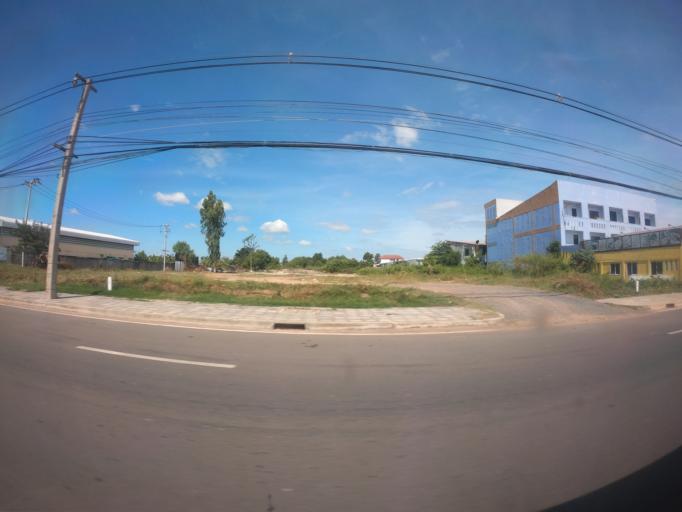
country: TH
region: Surin
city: Prasat
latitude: 14.6276
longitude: 103.4096
